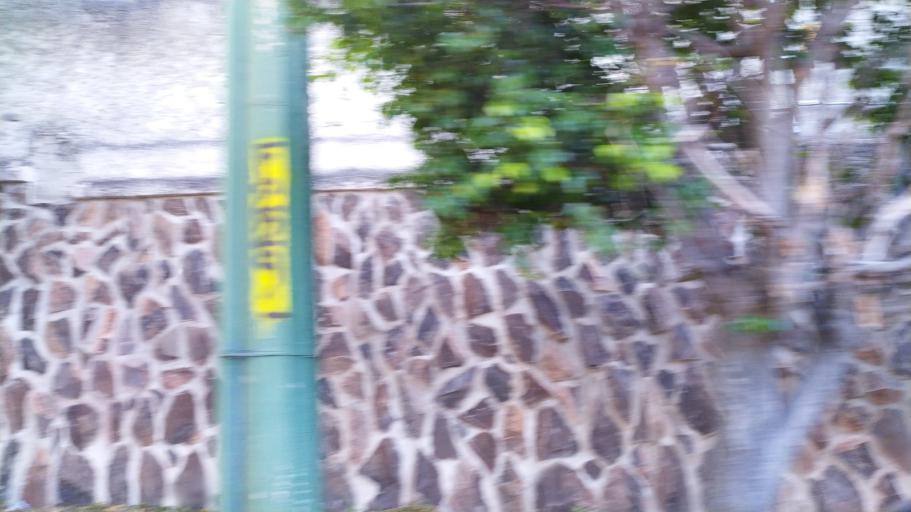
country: MX
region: Jalisco
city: Zapopan2
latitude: 20.7086
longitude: -103.4212
